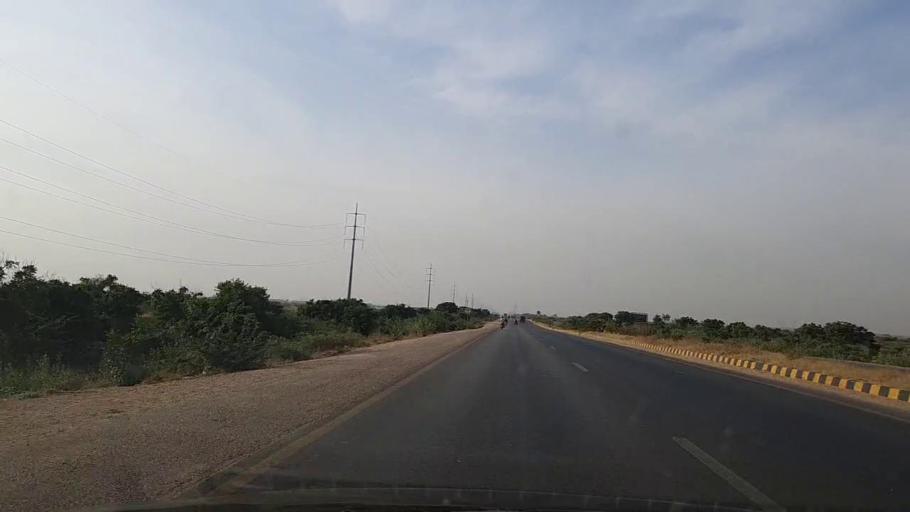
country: PK
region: Sindh
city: Gharo
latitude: 24.7715
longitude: 67.5463
